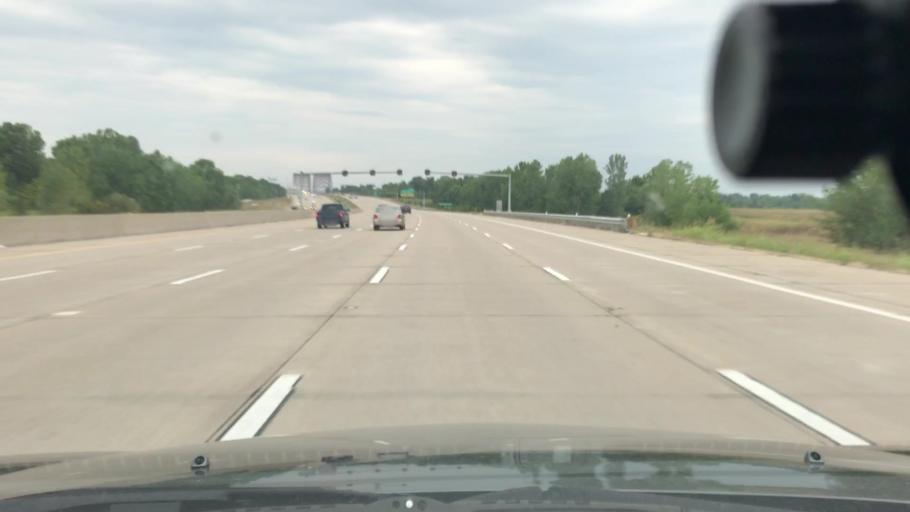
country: US
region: Missouri
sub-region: Saint Charles County
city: Saint Charles
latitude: 38.7255
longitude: -90.5137
